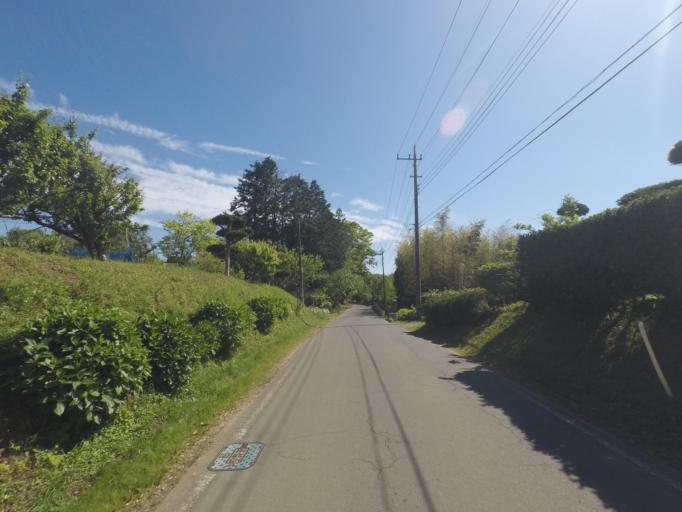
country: JP
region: Ibaraki
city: Itako
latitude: 36.0233
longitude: 140.4716
